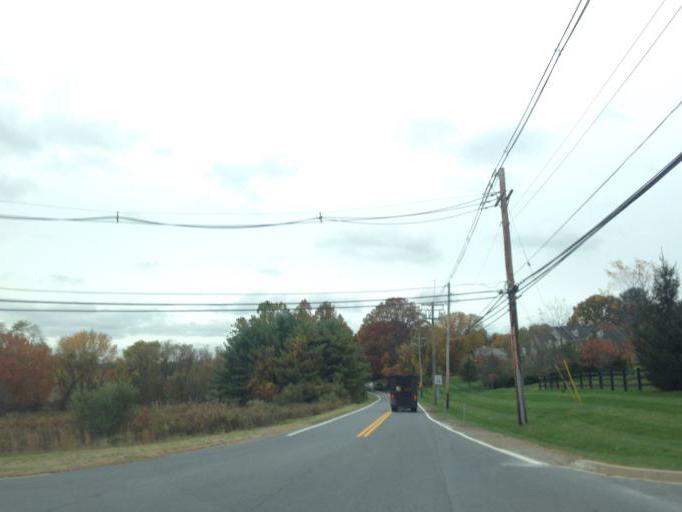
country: US
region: Maryland
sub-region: Baltimore County
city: Owings Mills
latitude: 39.4471
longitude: -76.7669
